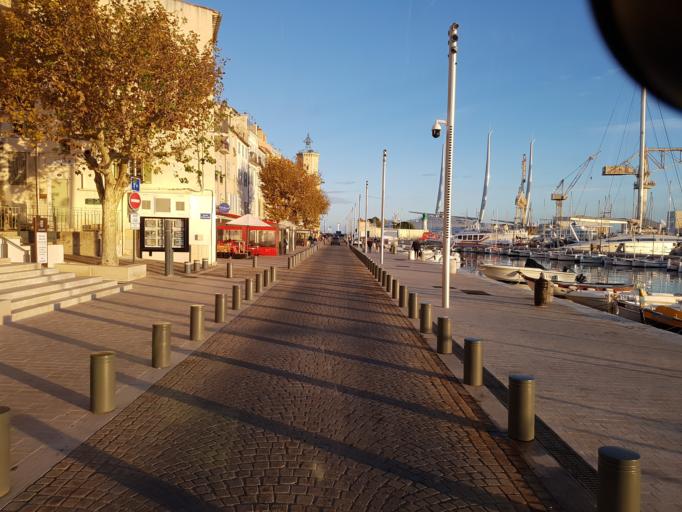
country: FR
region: Provence-Alpes-Cote d'Azur
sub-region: Departement des Bouches-du-Rhone
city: La Ciotat
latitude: 43.1745
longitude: 5.6079
